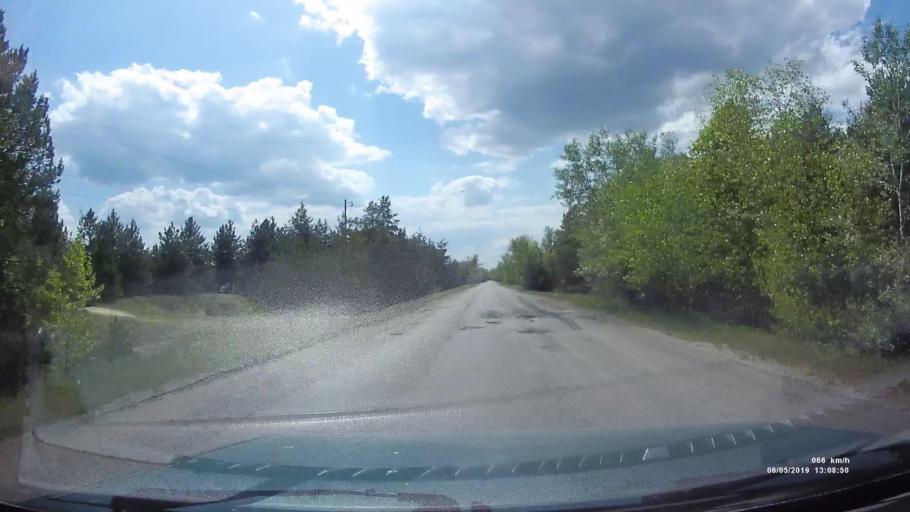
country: RU
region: Rostov
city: Ust'-Donetskiy
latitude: 47.7730
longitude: 40.9912
